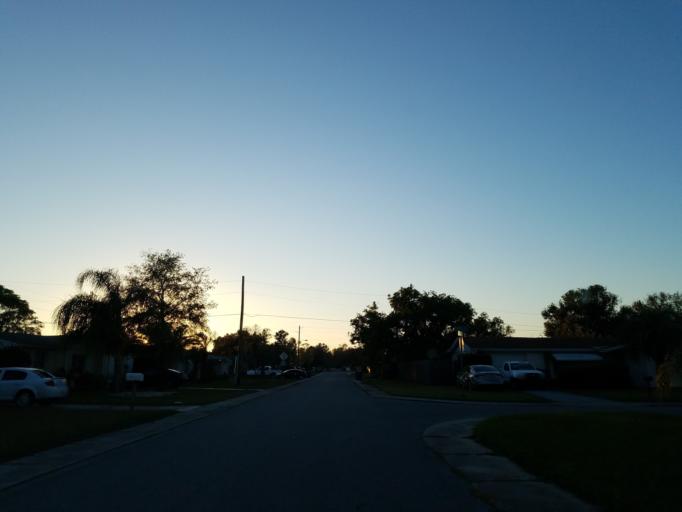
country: US
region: Florida
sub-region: Pasco County
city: Beacon Square
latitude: 28.2056
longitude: -82.7579
